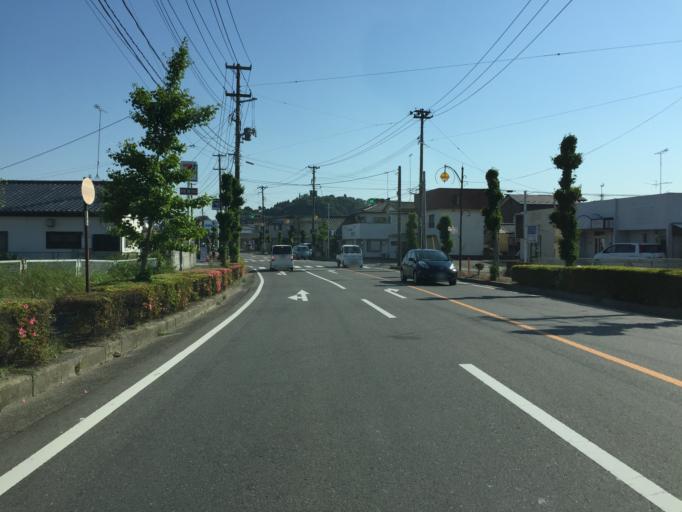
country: JP
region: Ibaraki
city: Kitaibaraki
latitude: 36.9165
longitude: 140.7757
